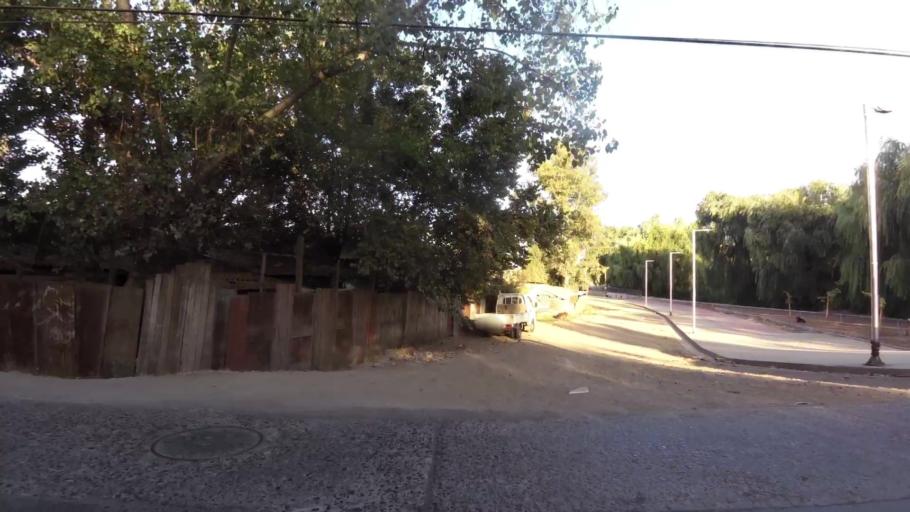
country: CL
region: Maule
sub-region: Provincia de Talca
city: Talca
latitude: -35.4403
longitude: -71.6472
